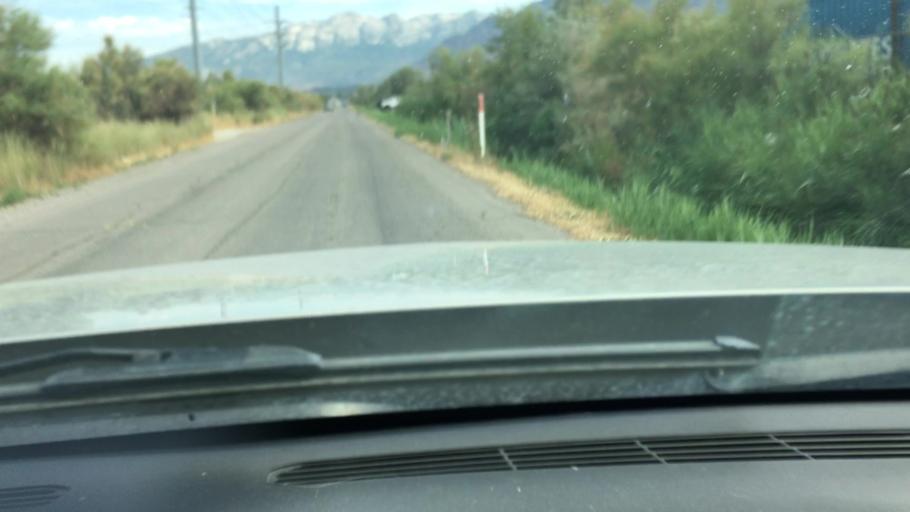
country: US
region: Utah
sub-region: Utah County
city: Pleasant Grove
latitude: 40.3343
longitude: -111.7599
